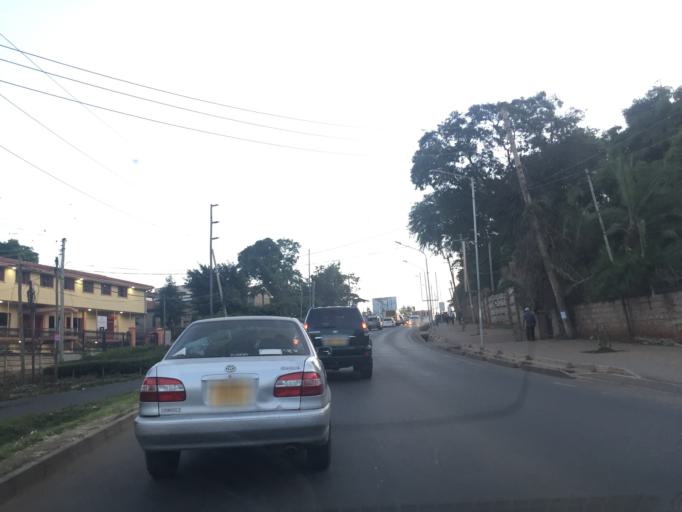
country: KE
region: Nairobi Area
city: Nairobi
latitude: -1.2697
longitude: 36.8018
